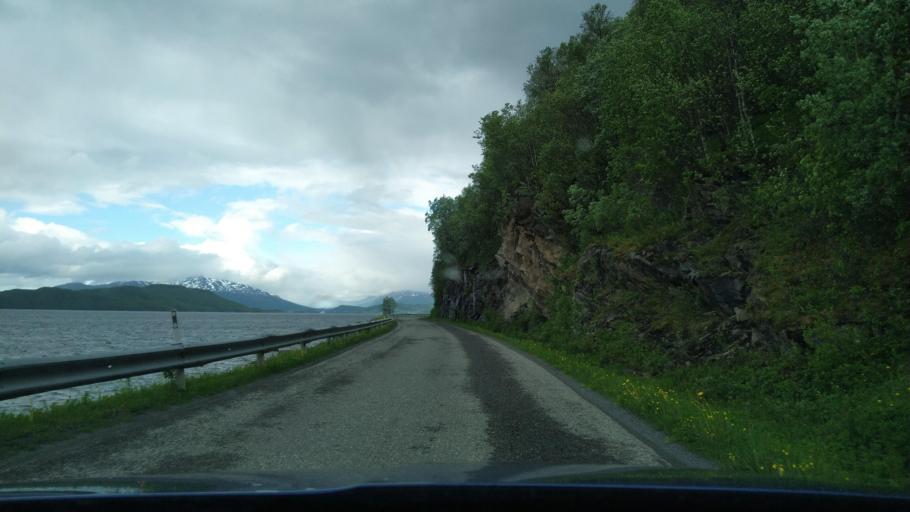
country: NO
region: Troms
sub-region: Lenvik
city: Finnsnes
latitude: 69.1408
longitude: 17.9124
